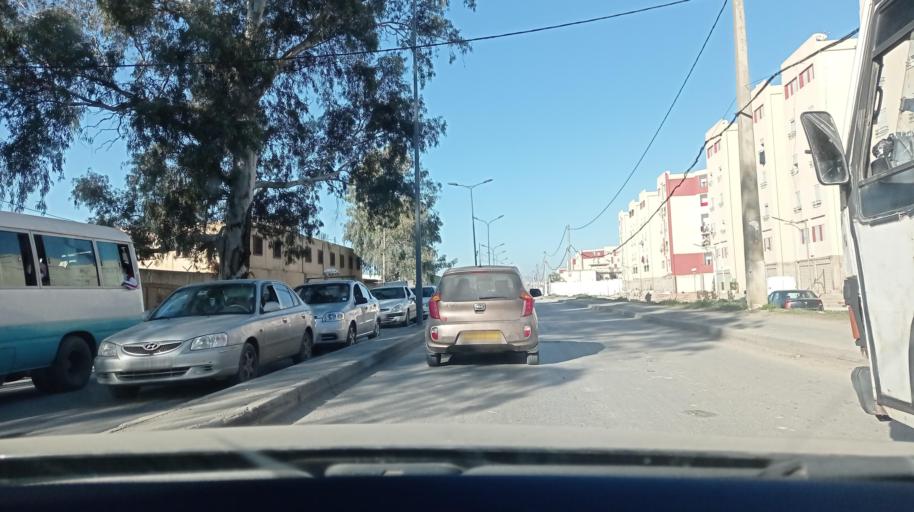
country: DZ
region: Tipaza
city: Baraki
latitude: 36.6587
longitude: 3.0855
